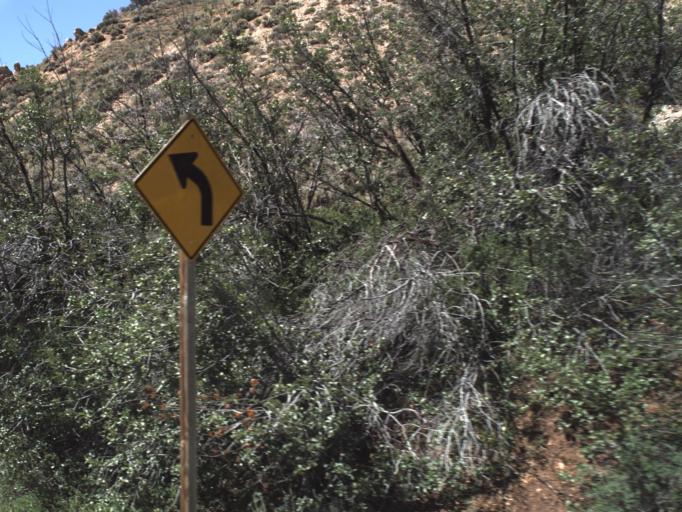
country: US
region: Utah
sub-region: Rich County
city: Randolph
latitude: 41.4818
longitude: -111.3733
